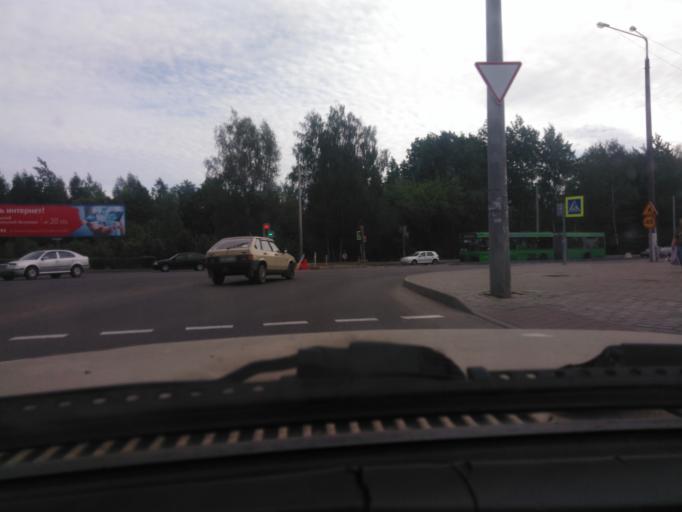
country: BY
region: Mogilev
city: Mahilyow
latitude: 53.9199
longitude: 30.2865
